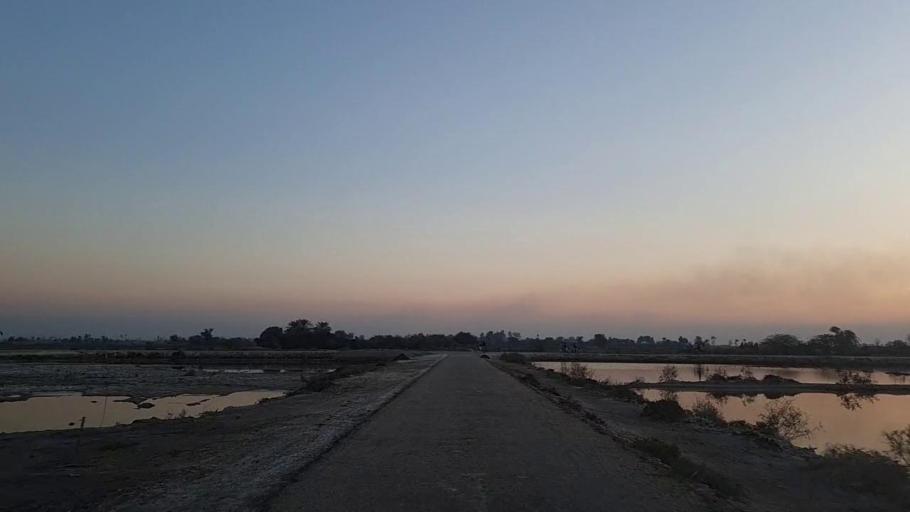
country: PK
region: Sindh
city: Bandhi
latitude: 26.5894
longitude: 68.3359
